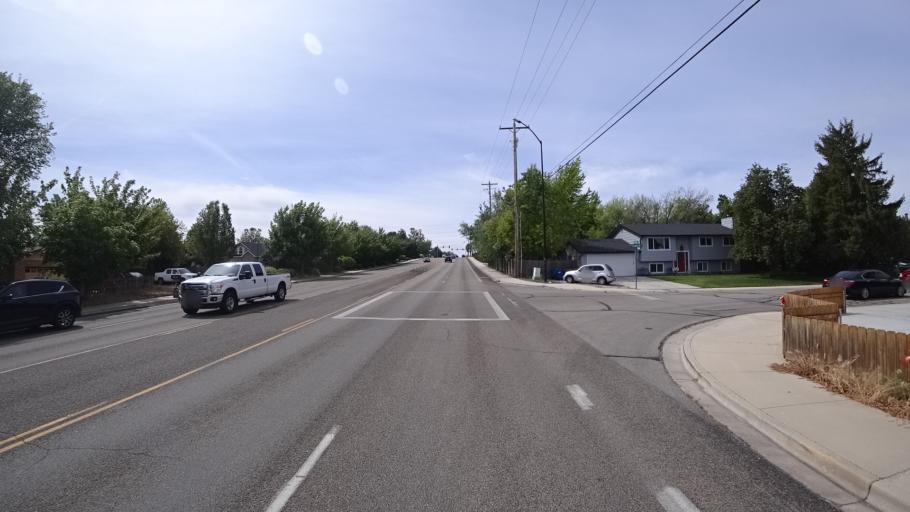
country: US
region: Idaho
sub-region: Ada County
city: Meridian
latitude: 43.5779
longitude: -116.3143
